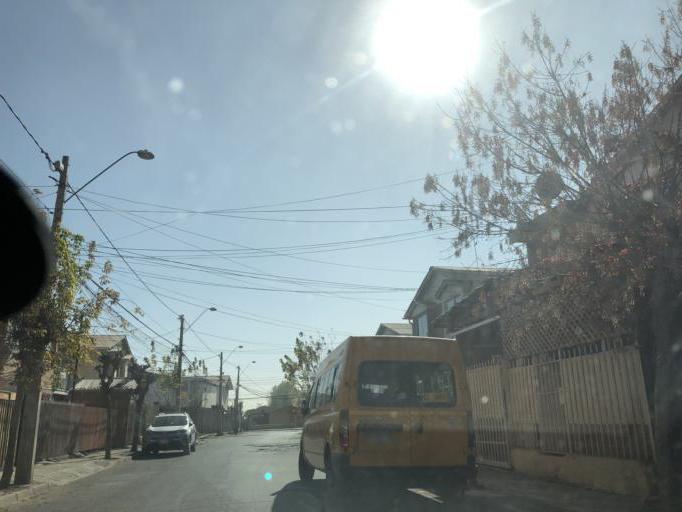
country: CL
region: Santiago Metropolitan
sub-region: Provincia de Cordillera
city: Puente Alto
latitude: -33.6109
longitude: -70.5894
